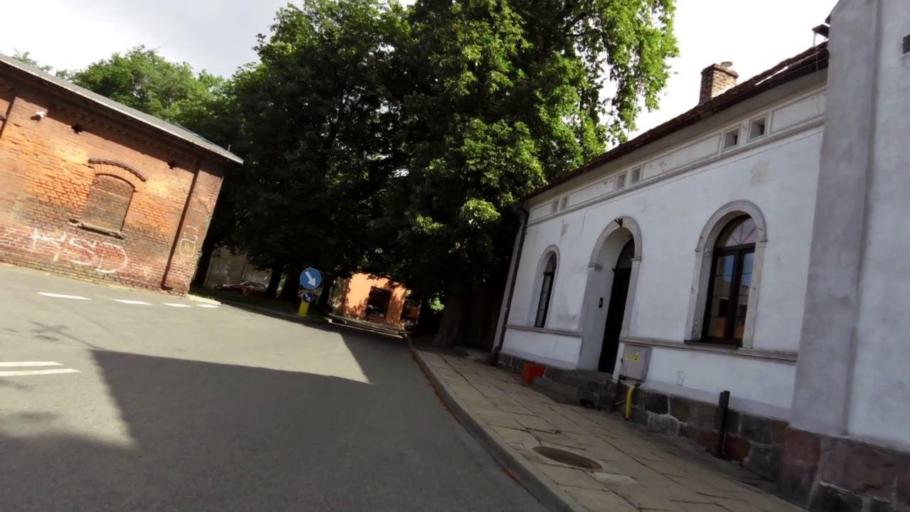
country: PL
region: West Pomeranian Voivodeship
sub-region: Powiat slawienski
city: Darlowo
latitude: 54.4242
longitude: 16.4148
